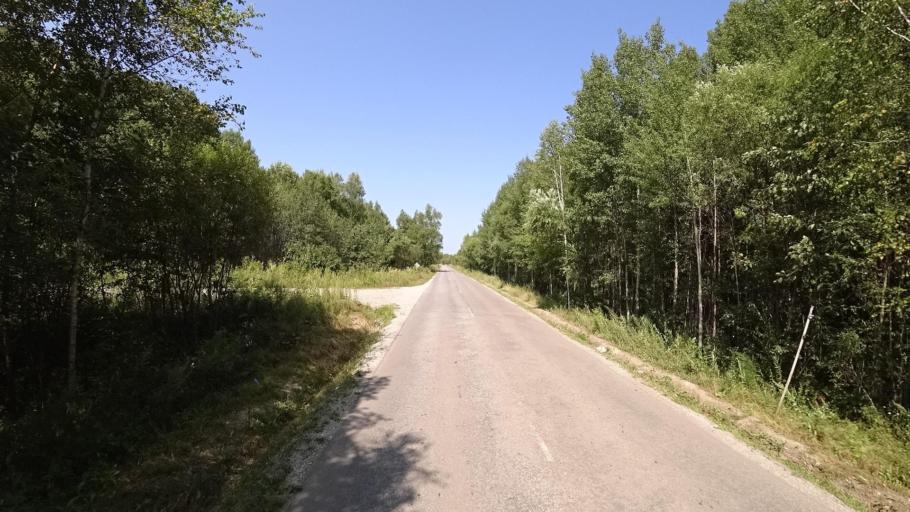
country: RU
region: Khabarovsk Krai
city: Khor
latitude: 47.9729
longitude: 135.1148
